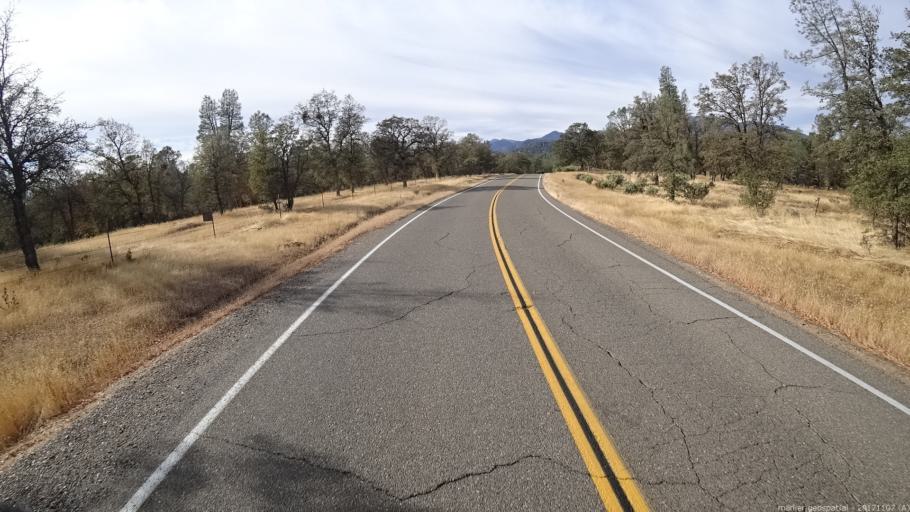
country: US
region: California
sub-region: Shasta County
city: Shasta
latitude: 40.5001
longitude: -122.5258
